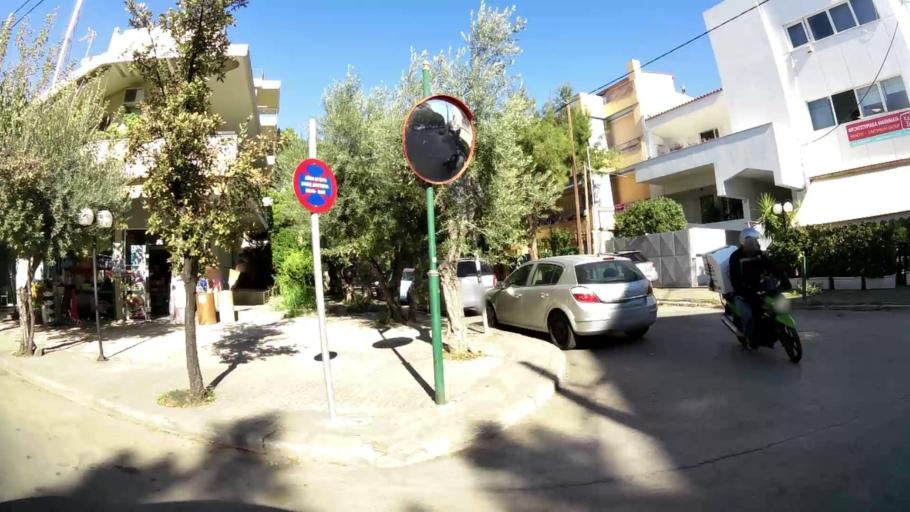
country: GR
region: Attica
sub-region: Nomarchia Athinas
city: Nea Erythraia
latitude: 38.0900
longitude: 23.8150
